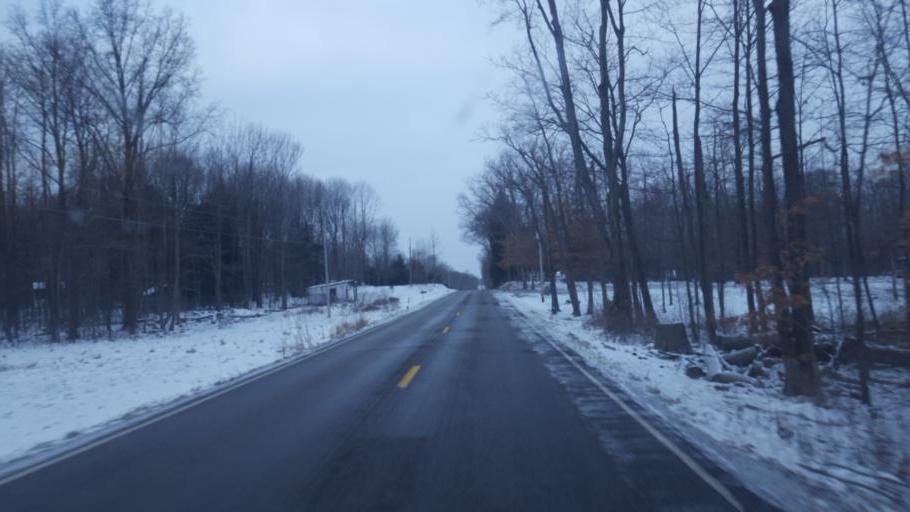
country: US
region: Pennsylvania
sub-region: Mercer County
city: Stoneboro
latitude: 41.4057
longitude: -80.0233
